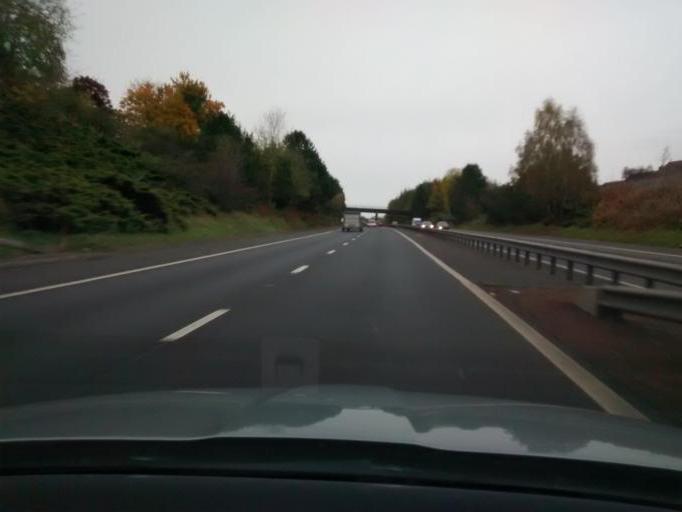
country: GB
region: Scotland
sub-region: Stirling
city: Stirling
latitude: 56.1125
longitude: -3.9646
